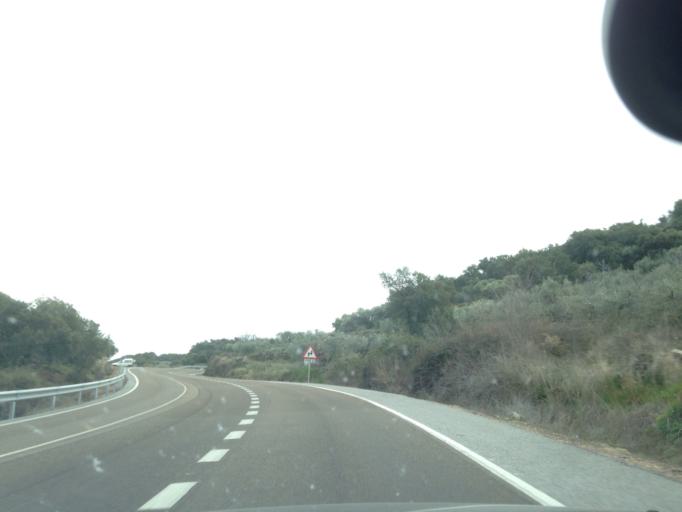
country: ES
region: Extremadura
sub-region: Provincia de Caceres
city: Montanchez
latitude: 39.2312
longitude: -6.1587
